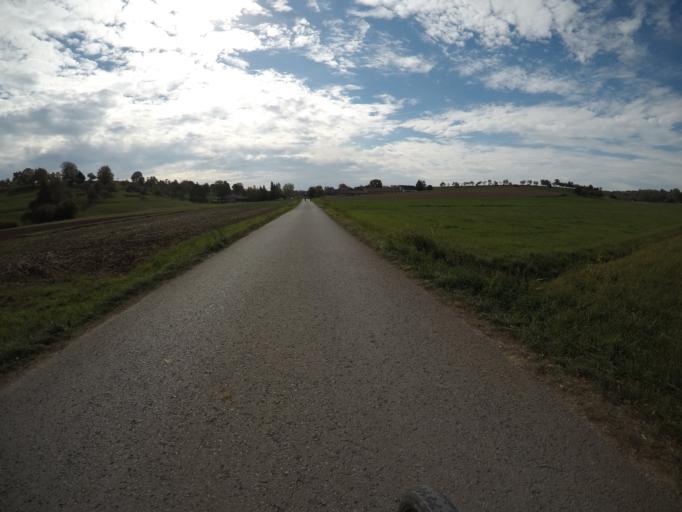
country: DE
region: Baden-Wuerttemberg
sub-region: Regierungsbezirk Stuttgart
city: Hildrizhausen
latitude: 48.6341
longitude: 8.9698
